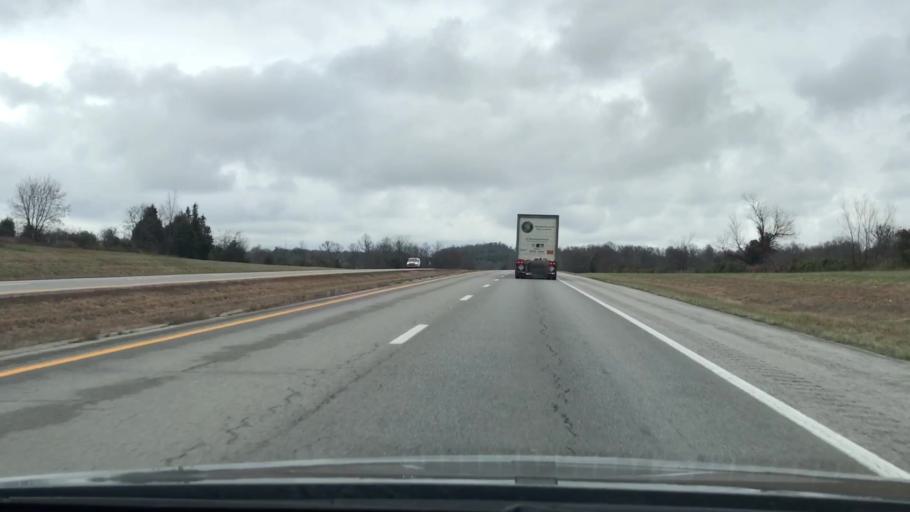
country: US
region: Kentucky
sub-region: Christian County
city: Hopkinsville
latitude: 36.9251
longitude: -87.4719
